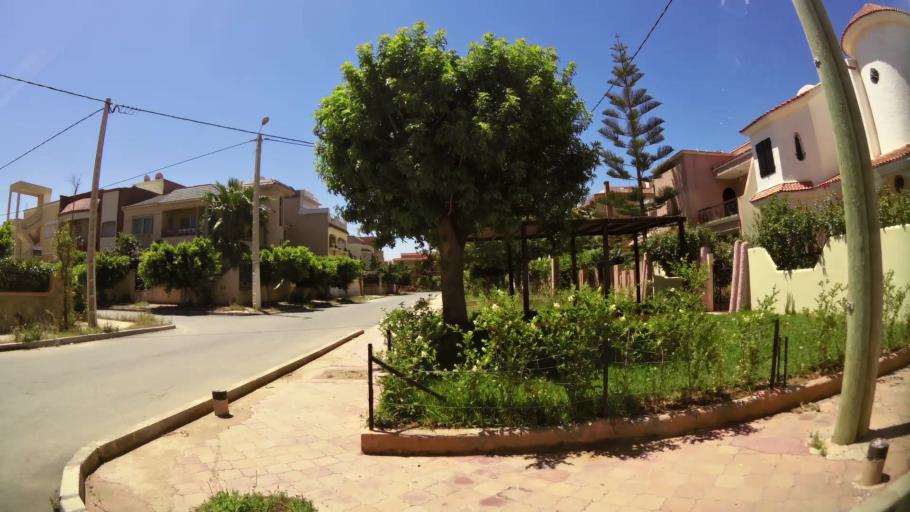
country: MA
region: Oriental
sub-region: Berkane-Taourirt
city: Madagh
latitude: 35.0862
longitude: -2.2389
